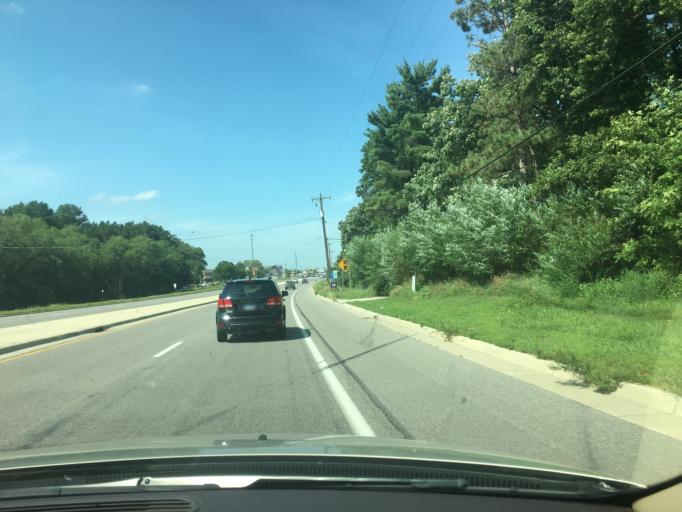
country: US
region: Minnesota
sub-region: Stearns County
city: Saint Augusta
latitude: 45.5111
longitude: -94.1583
